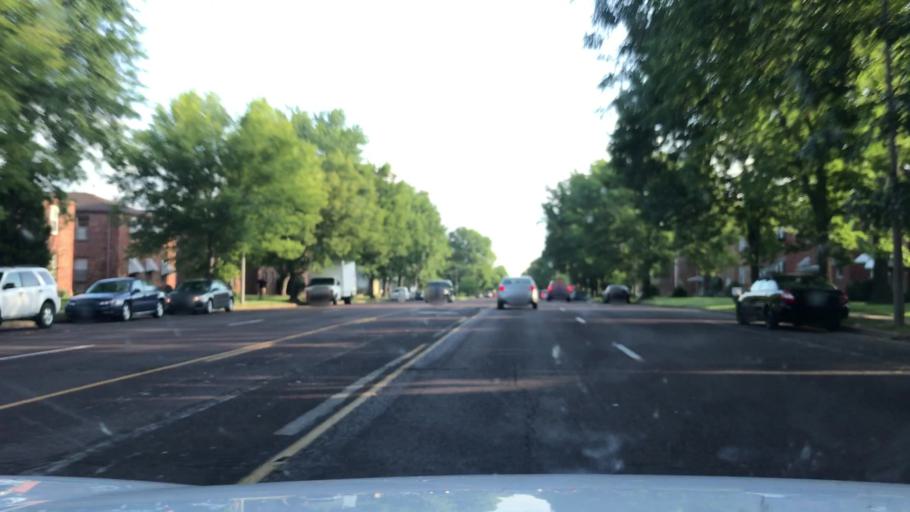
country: US
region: Missouri
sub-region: Saint Louis County
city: Maplewood
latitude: 38.5939
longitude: -90.3093
